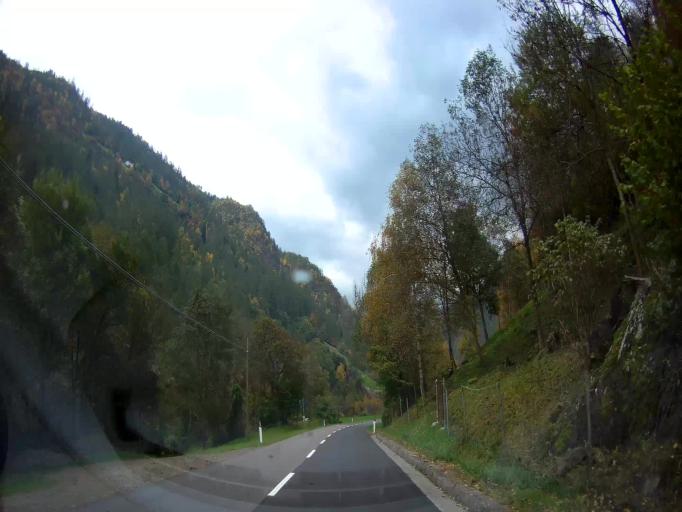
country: IT
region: Trentino-Alto Adige
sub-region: Bolzano
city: Certosa
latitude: 46.6817
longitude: 10.9355
